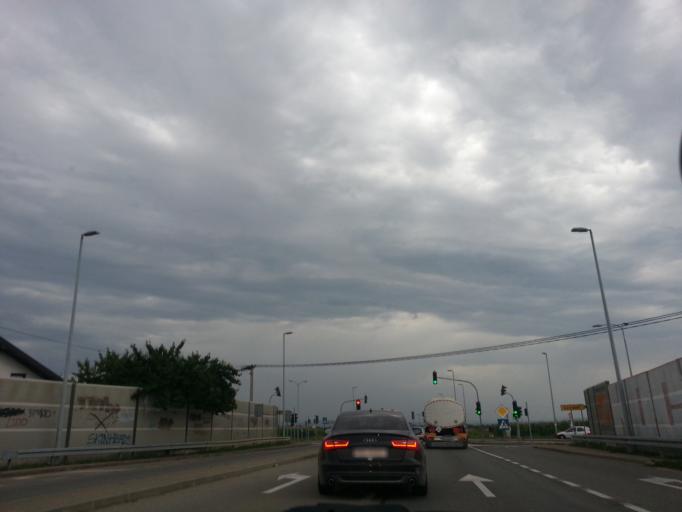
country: BA
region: Republika Srpska
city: Bijeljina
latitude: 44.7789
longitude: 19.2252
